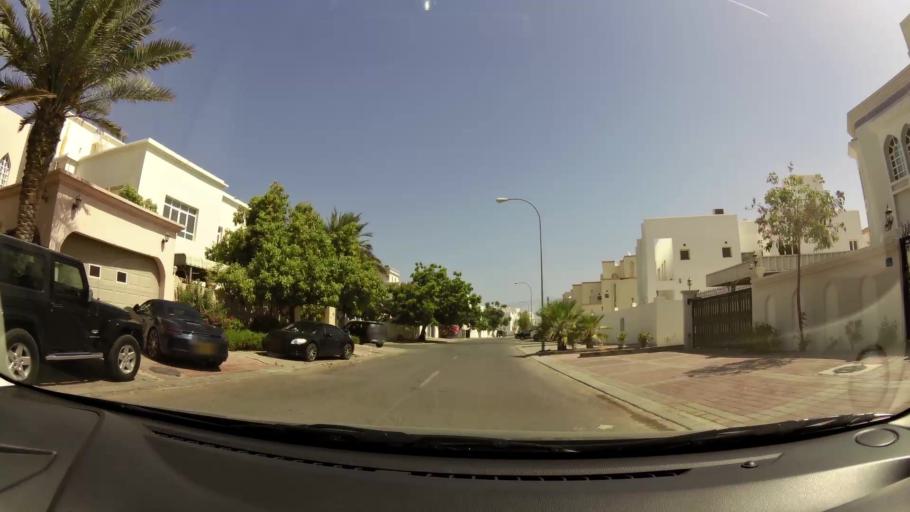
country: OM
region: Muhafazat Masqat
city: Bawshar
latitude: 23.5955
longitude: 58.4039
